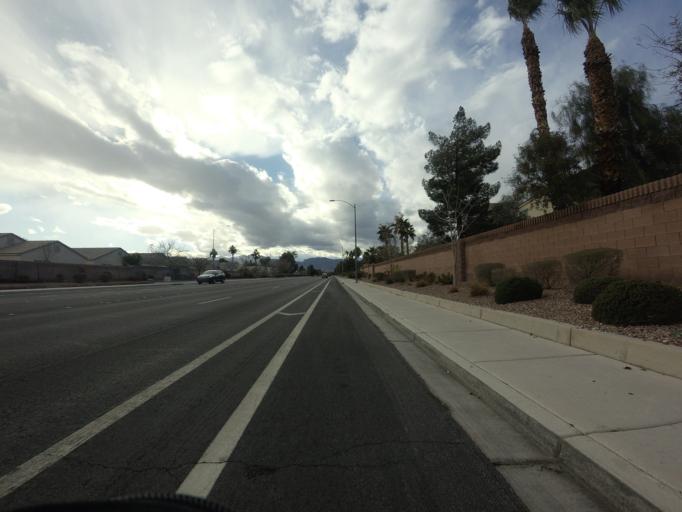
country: US
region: Nevada
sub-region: Clark County
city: North Las Vegas
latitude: 36.2684
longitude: -115.2179
